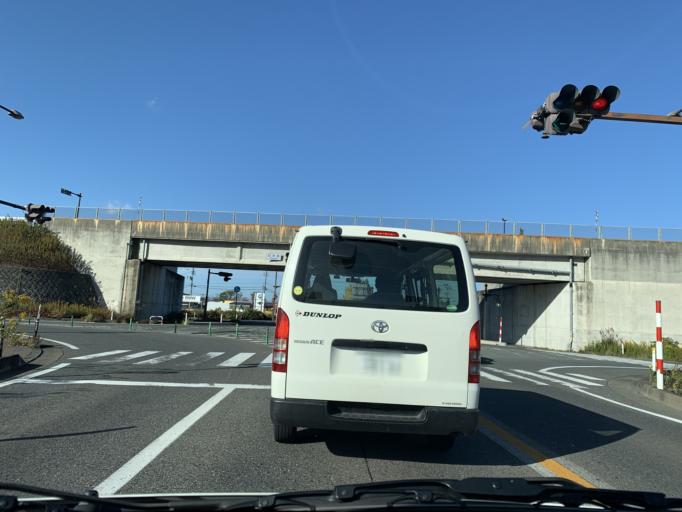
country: JP
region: Iwate
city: Mizusawa
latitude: 39.1685
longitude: 141.1422
